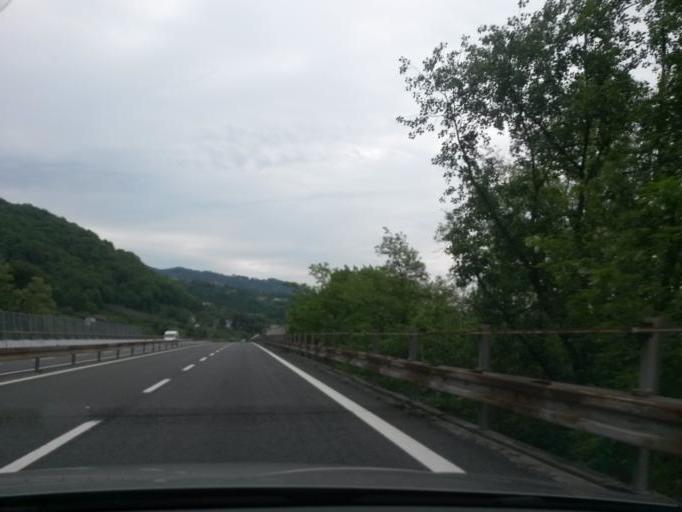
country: IT
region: Liguria
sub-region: Provincia di La Spezia
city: Piana Battolla
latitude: 44.1989
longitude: 9.8481
